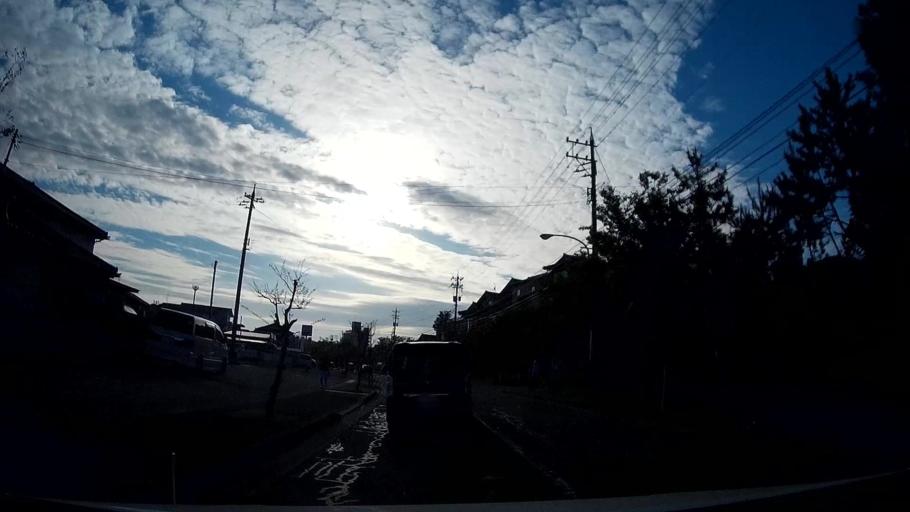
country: JP
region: Ishikawa
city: Nanao
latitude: 37.0839
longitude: 136.9319
